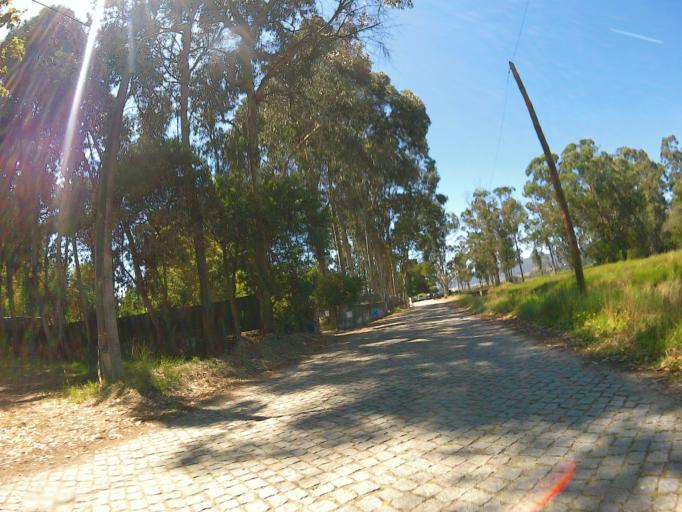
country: PT
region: Viana do Castelo
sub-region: Viana do Castelo
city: Darque
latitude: 41.6917
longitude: -8.7722
